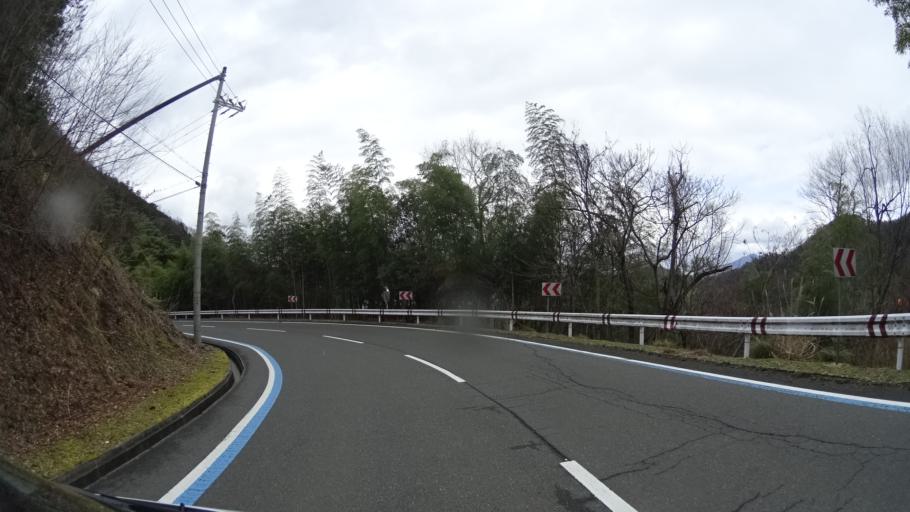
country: JP
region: Kyoto
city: Maizuru
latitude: 35.4358
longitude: 135.4007
